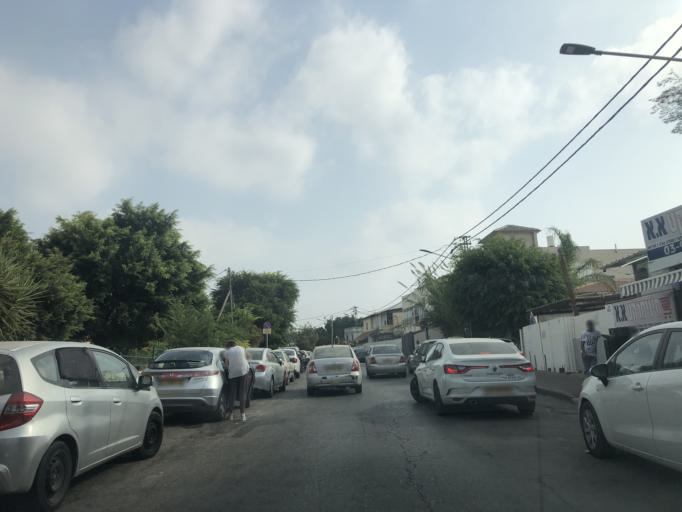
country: IL
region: Central District
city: Rosh Ha'Ayin
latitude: 32.0958
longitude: 34.9506
